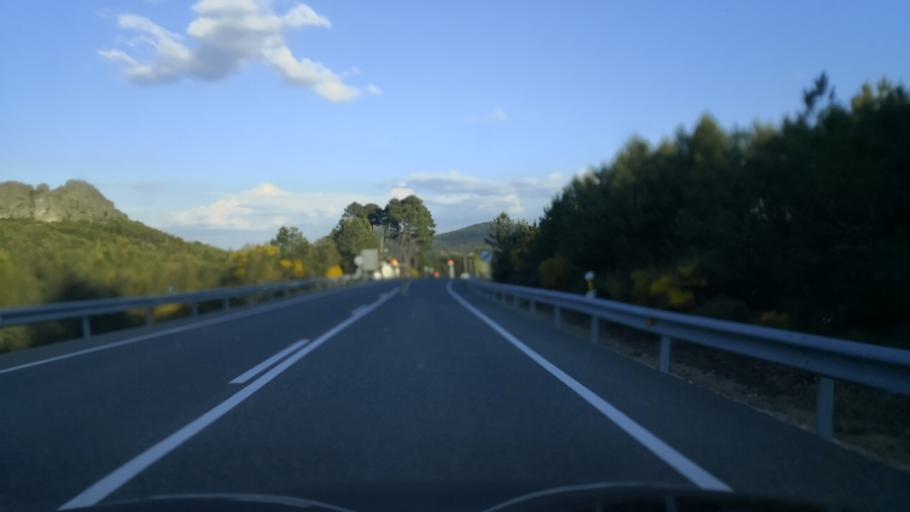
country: PT
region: Portalegre
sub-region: Portalegre
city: Sao Juliao
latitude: 39.3476
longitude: -7.3004
